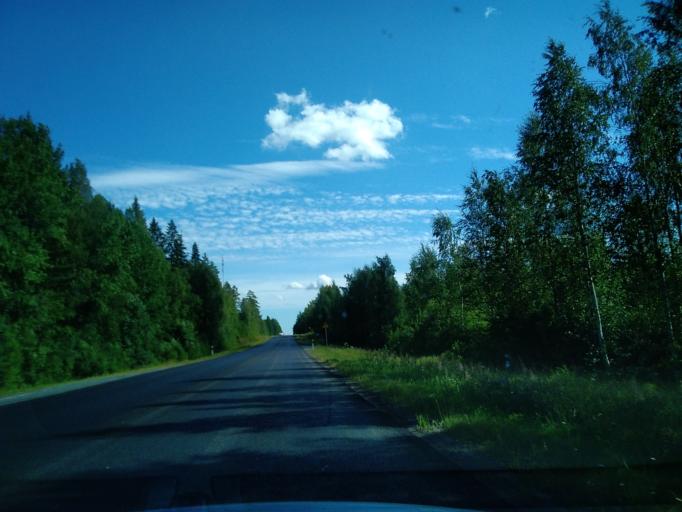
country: FI
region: Haeme
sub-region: Haemeenlinna
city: Renko
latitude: 60.9337
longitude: 24.3660
